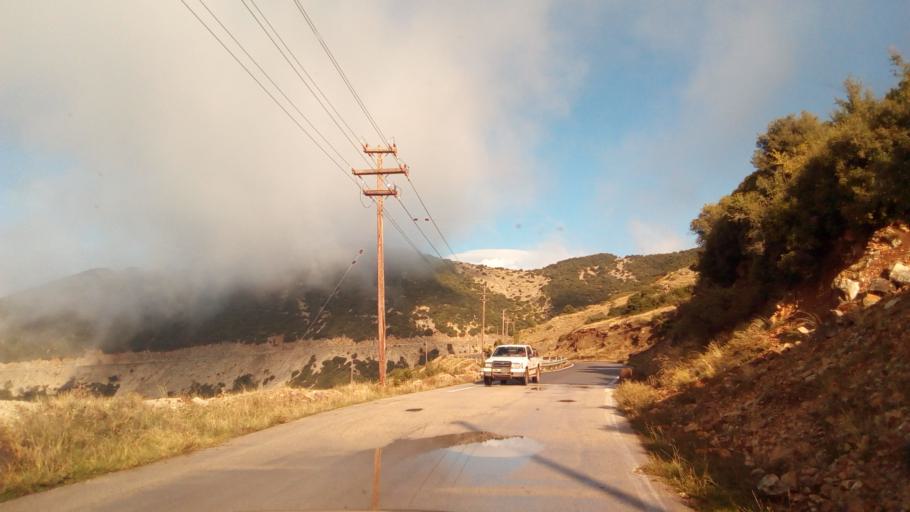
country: GR
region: West Greece
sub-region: Nomos Aitolias kai Akarnanias
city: Thermo
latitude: 38.5833
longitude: 21.7746
